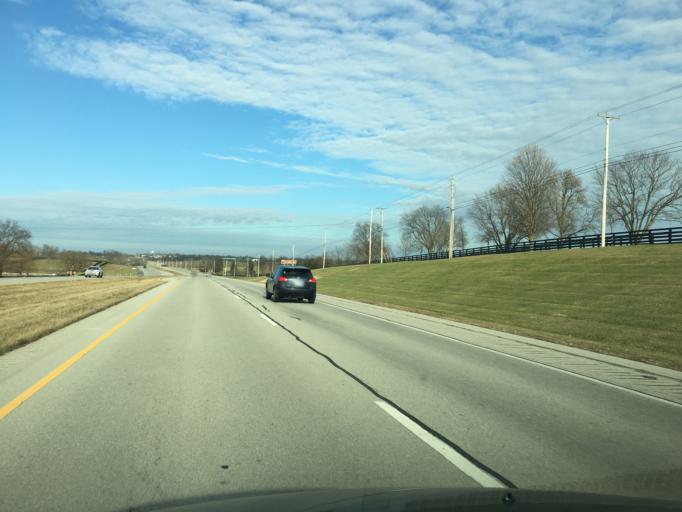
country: US
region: Kentucky
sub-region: Scott County
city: Georgetown
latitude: 38.1783
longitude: -84.5960
